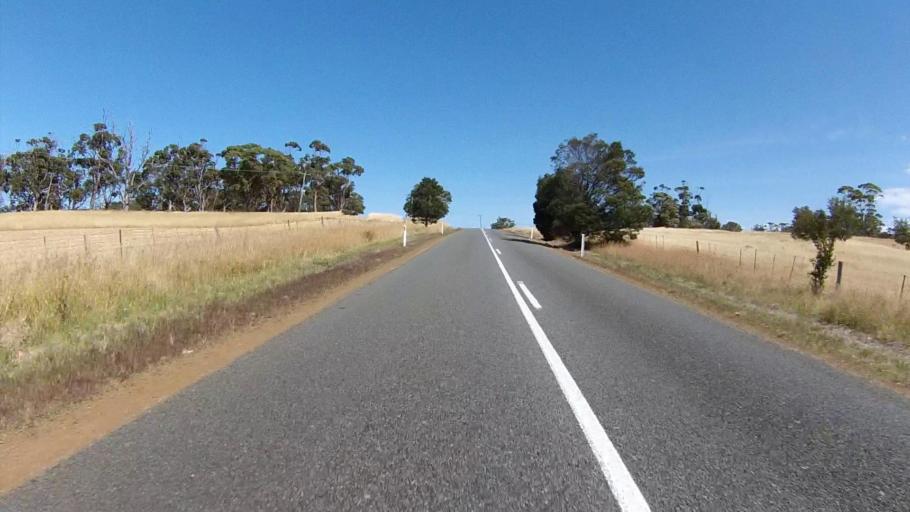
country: AU
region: Tasmania
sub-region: Sorell
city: Sorell
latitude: -42.2813
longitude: 147.9995
